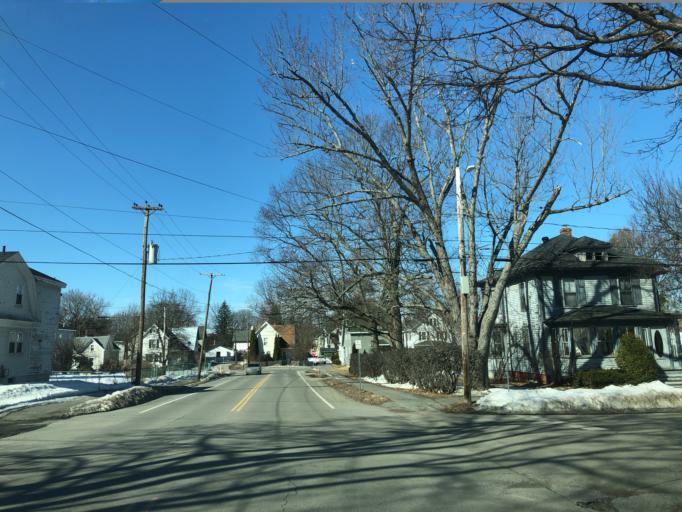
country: US
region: Maine
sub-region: Penobscot County
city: Brewer
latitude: 44.8124
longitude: -68.7654
